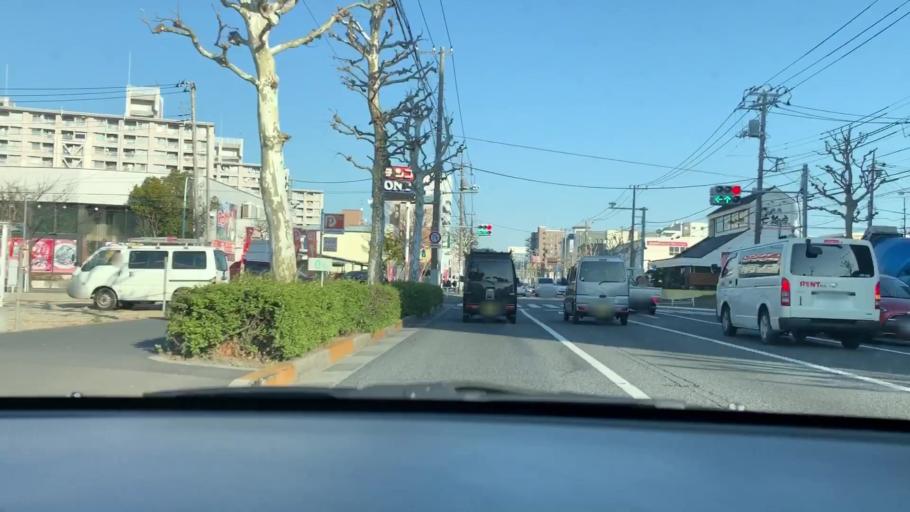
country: JP
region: Tokyo
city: Urayasu
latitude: 35.7021
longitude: 139.8896
